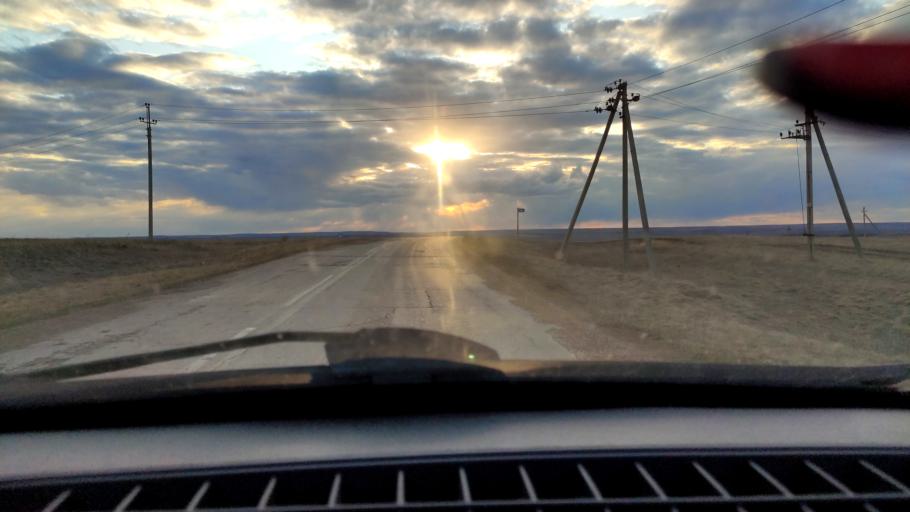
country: RU
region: Bashkortostan
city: Tolbazy
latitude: 54.0114
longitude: 55.5722
